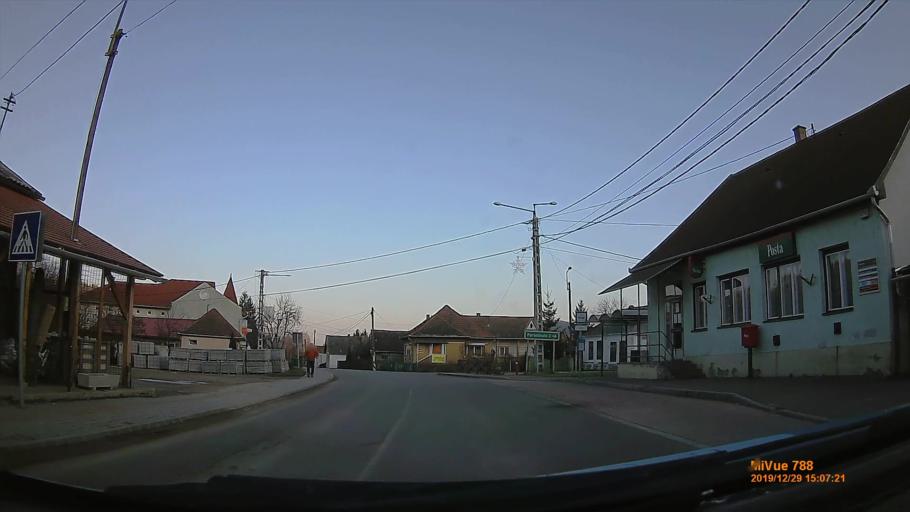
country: HU
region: Heves
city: Parad
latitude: 47.9232
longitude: 20.0293
